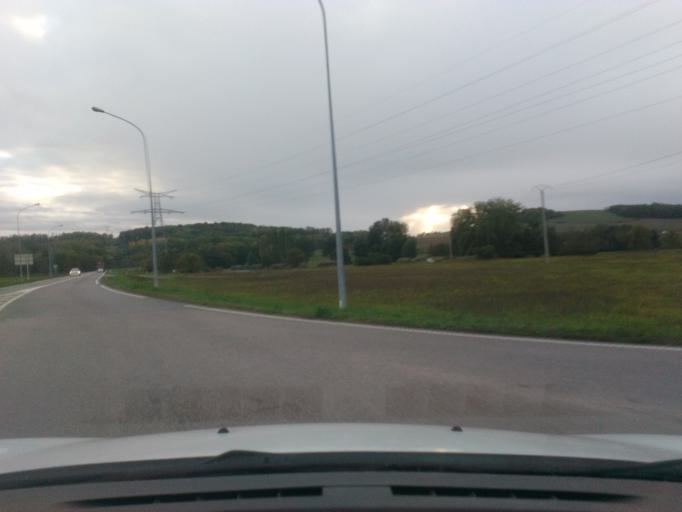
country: FR
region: Lorraine
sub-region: Departement des Vosges
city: Vincey
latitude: 48.3506
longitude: 6.3182
